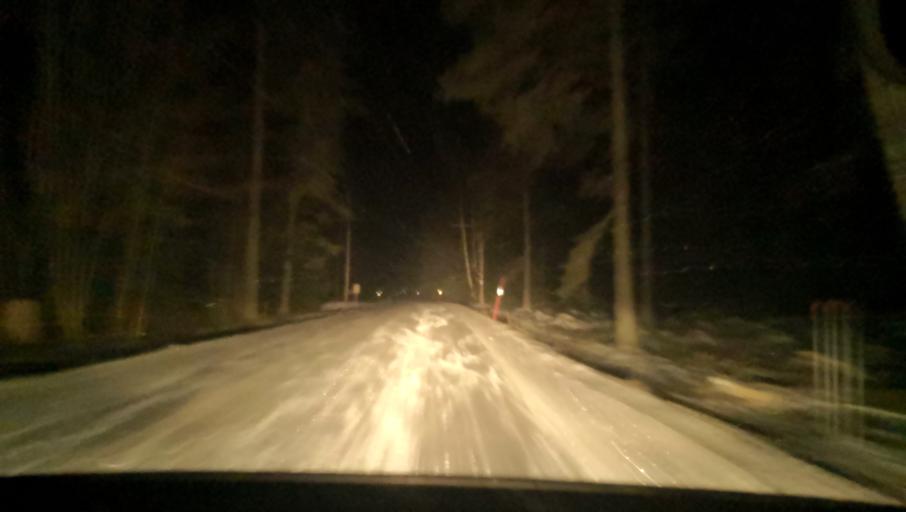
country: SE
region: Uppsala
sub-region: Heby Kommun
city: Tarnsjo
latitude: 60.1434
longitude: 16.9103
